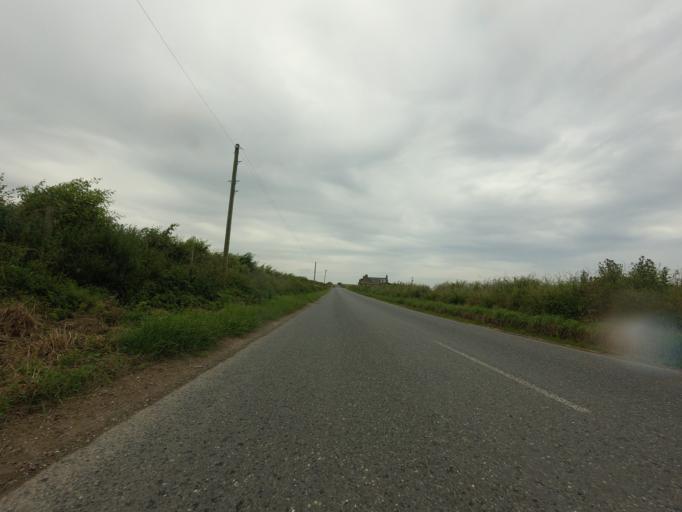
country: GB
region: Scotland
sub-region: Aberdeenshire
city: Whitehills
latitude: 57.6713
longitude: -2.6208
